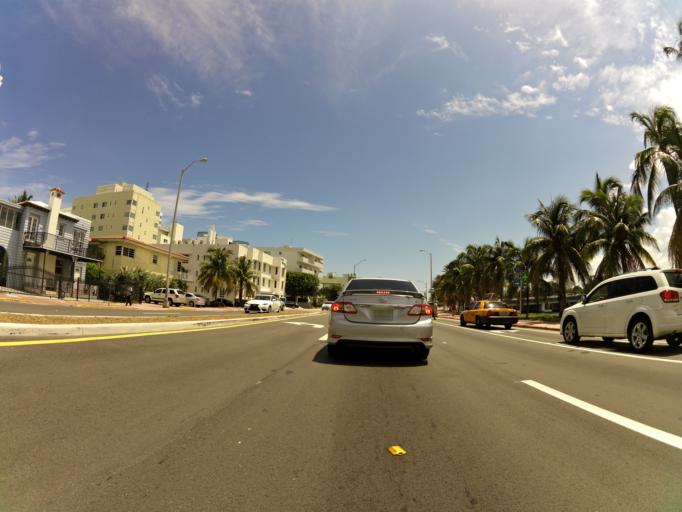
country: US
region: Florida
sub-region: Miami-Dade County
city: Miami Beach
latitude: 25.8143
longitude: -80.1237
